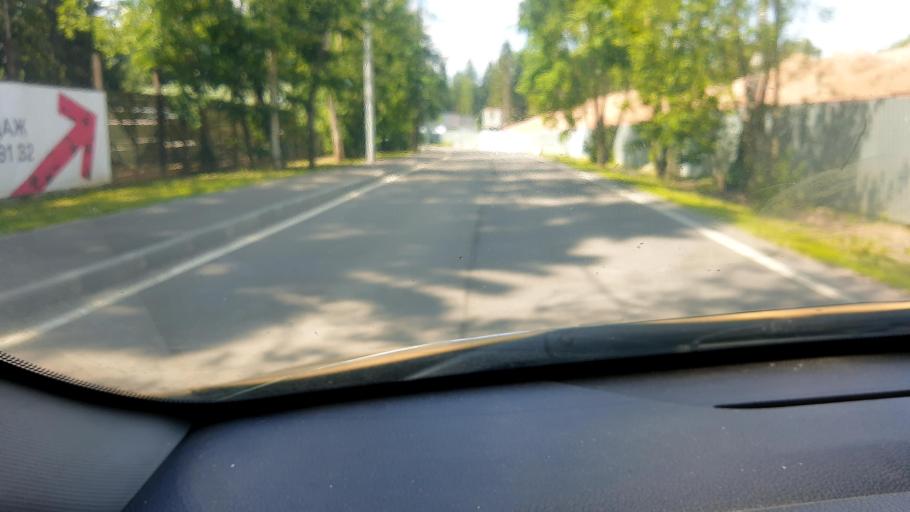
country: RU
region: Moskovskaya
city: Vatutinki
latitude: 55.5030
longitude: 37.3207
